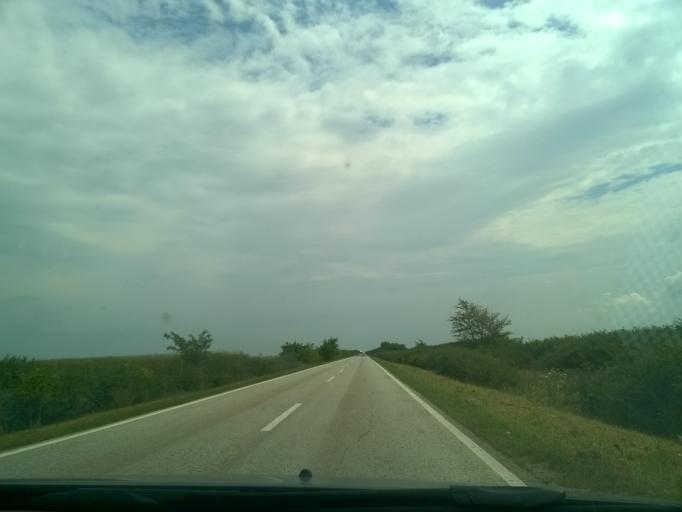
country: RS
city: Banatski Despotovac
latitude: 45.3845
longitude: 20.6399
